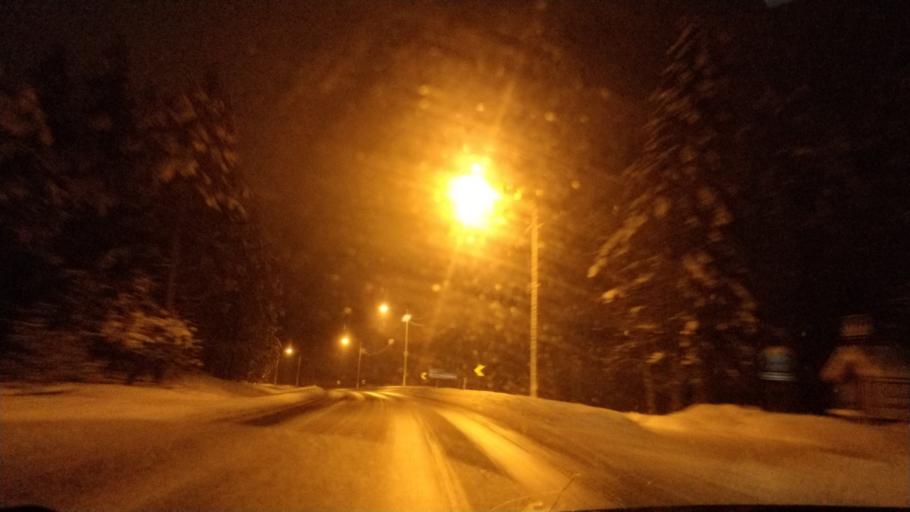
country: FI
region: Lapland
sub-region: Rovaniemi
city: Rovaniemi
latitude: 66.2744
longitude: 25.3297
